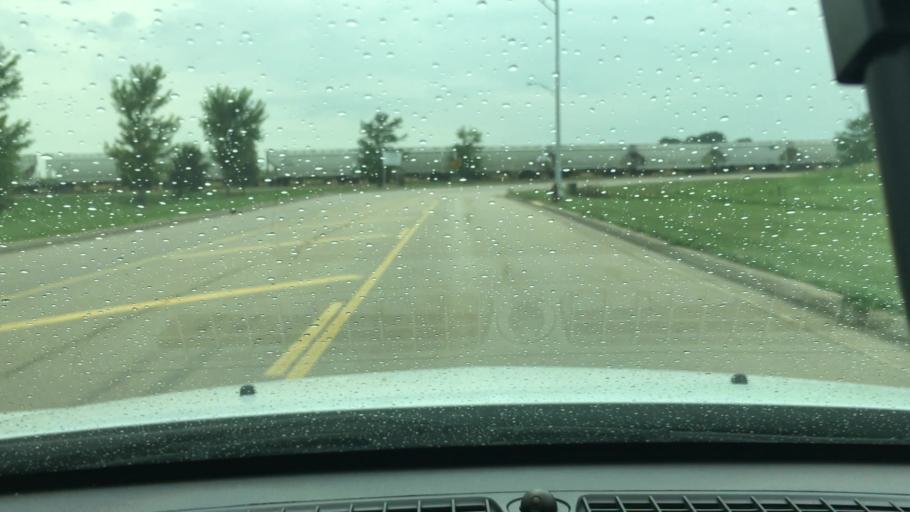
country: US
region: Illinois
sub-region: Ogle County
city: Rochelle
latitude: 41.8962
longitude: -89.0382
